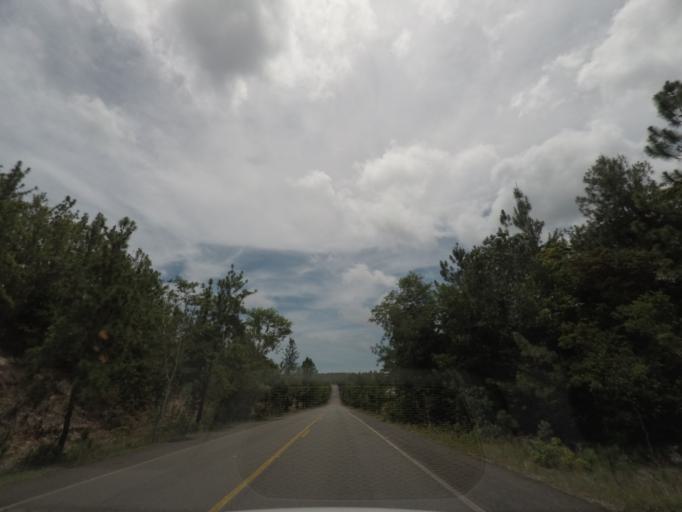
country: BR
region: Bahia
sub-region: Entre Rios
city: Entre Rios
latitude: -12.1239
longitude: -37.7897
